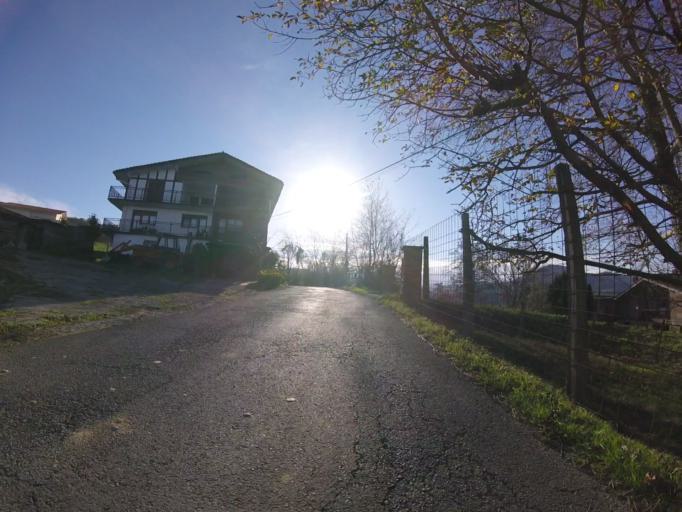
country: ES
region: Basque Country
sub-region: Provincia de Guipuzcoa
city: Astigarraga
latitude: 43.2642
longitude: -1.9415
